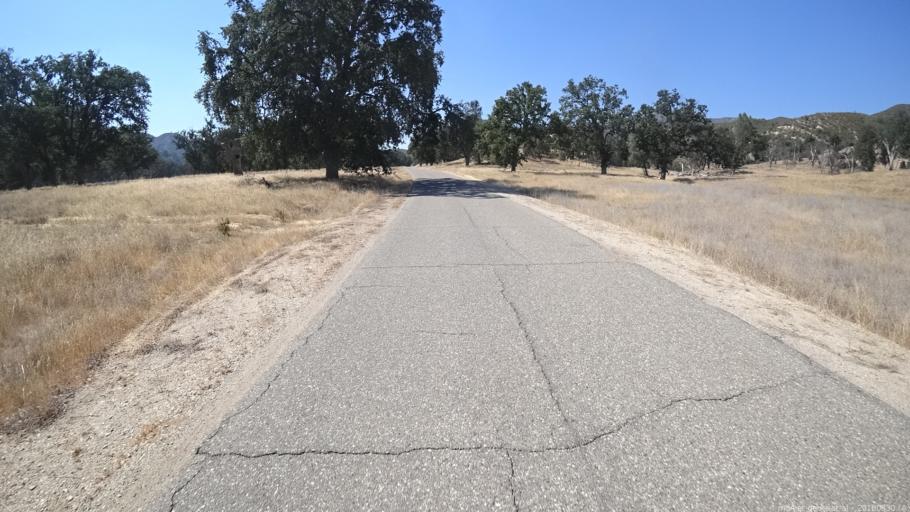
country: US
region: California
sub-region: Monterey County
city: King City
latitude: 36.0711
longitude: -121.3372
